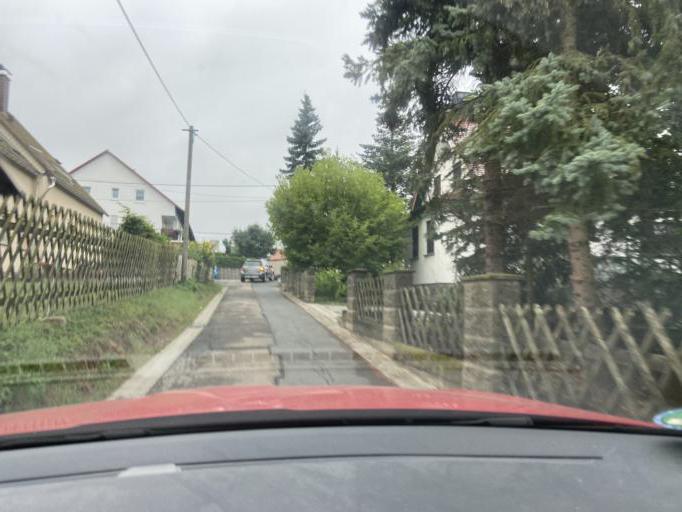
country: DE
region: Saxony
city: Tharandt
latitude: 51.0166
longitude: 13.5707
